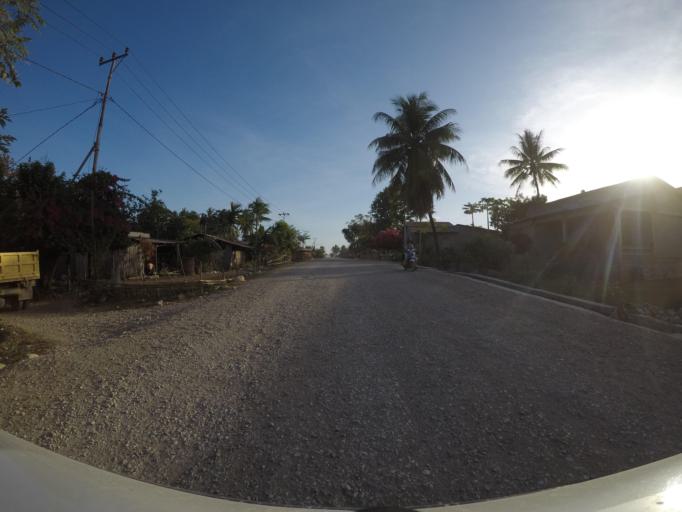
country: TL
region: Viqueque
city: Viqueque
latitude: -8.8256
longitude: 126.5289
